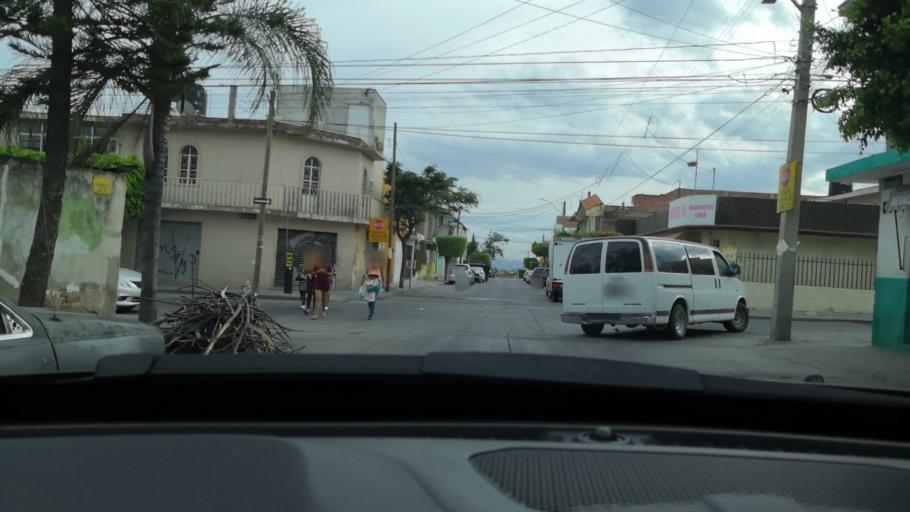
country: MX
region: Guanajuato
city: Leon
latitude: 21.1288
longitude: -101.7062
